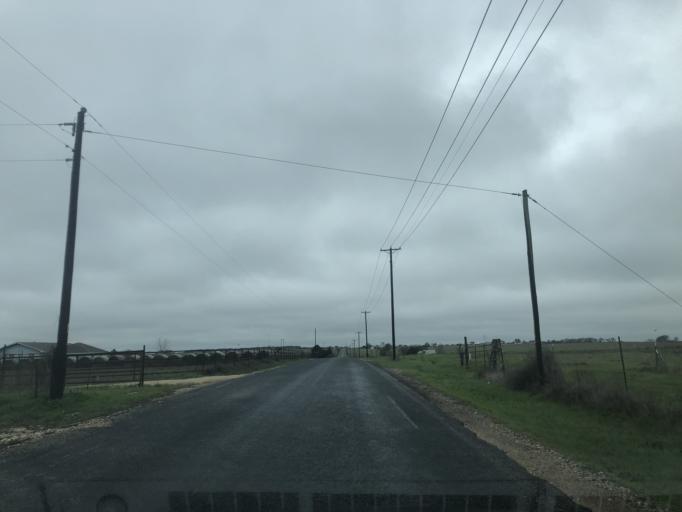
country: US
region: Texas
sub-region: Williamson County
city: Serenada
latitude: 30.7685
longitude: -97.6169
